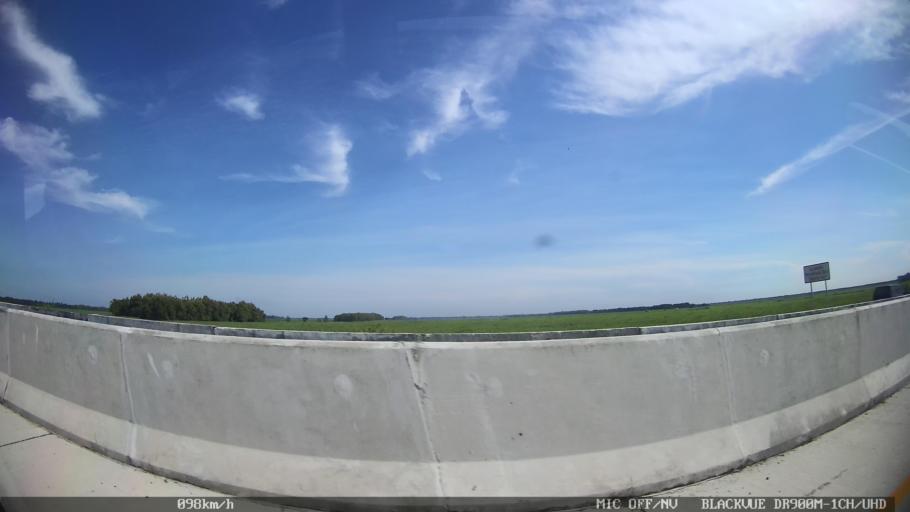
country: ID
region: North Sumatra
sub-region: Kabupaten Langkat
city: Stabat
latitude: 3.7135
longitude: 98.5196
